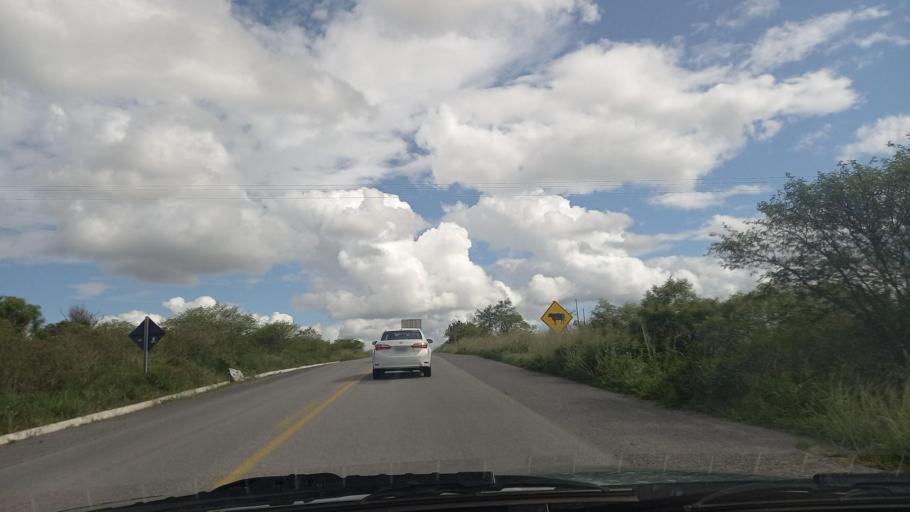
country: BR
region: Pernambuco
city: Garanhuns
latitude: -8.8178
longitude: -36.4470
